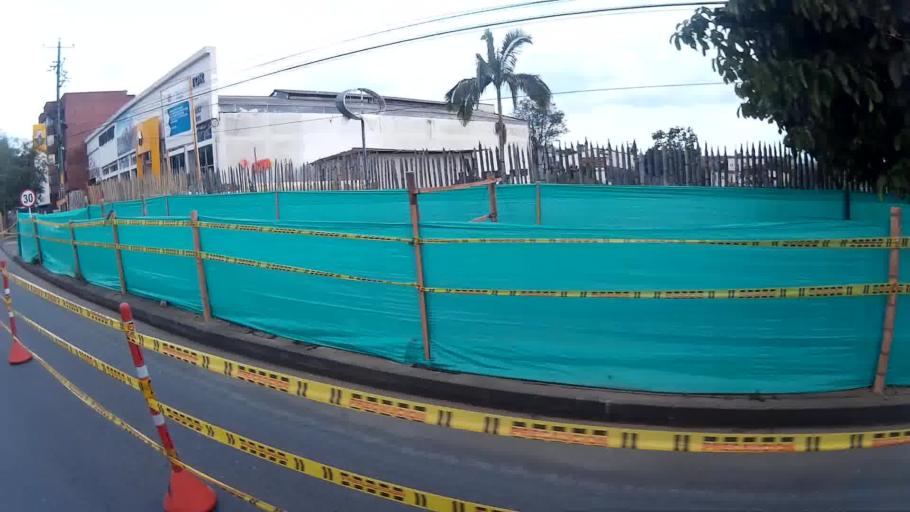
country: CO
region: Risaralda
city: Pereira
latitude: 4.8146
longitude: -75.7152
